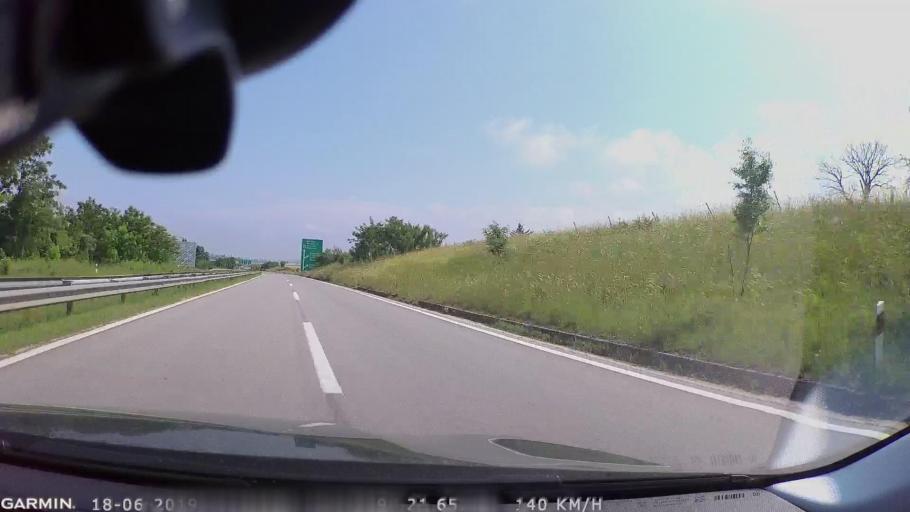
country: MK
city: Miladinovci
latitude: 41.9787
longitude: 21.6522
